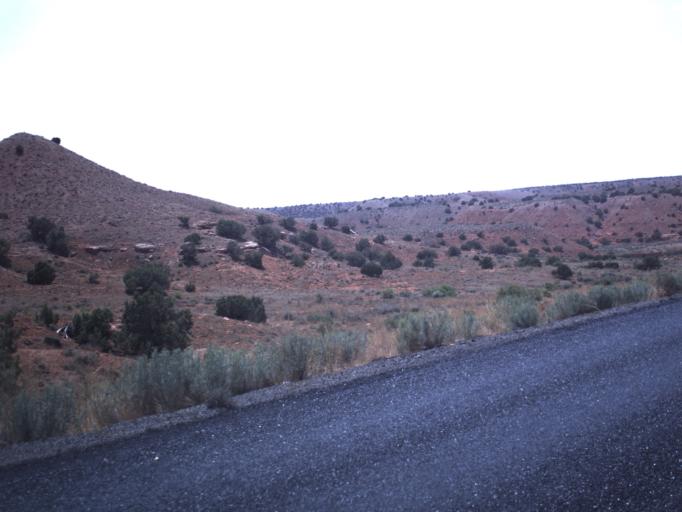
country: US
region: Utah
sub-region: Uintah County
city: Maeser
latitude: 40.4142
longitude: -109.6881
